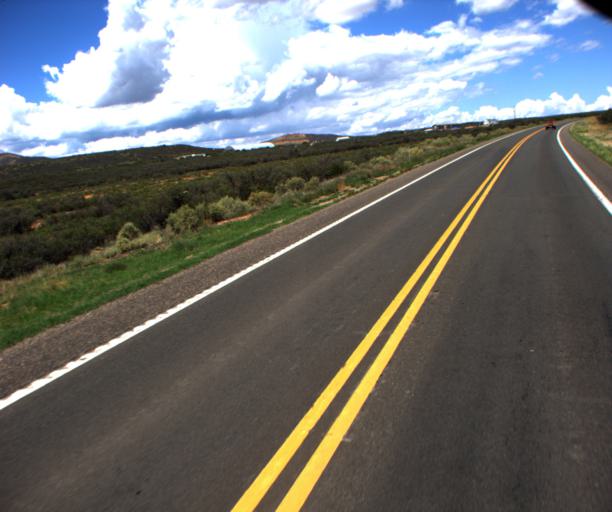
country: US
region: Arizona
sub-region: Yavapai County
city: Dewey-Humboldt
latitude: 34.5361
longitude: -112.1419
